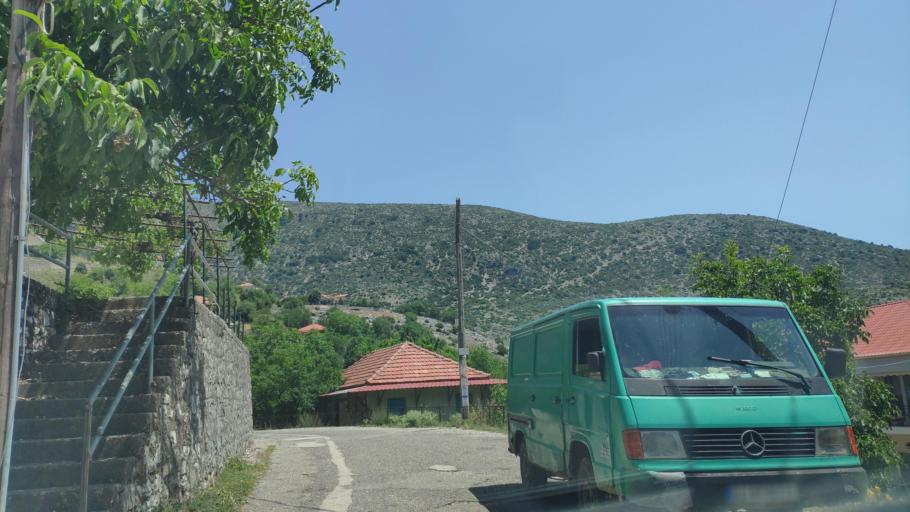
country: GR
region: West Greece
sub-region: Nomos Aitolias kai Akarnanias
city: Krikellos
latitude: 39.0490
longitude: 21.3631
